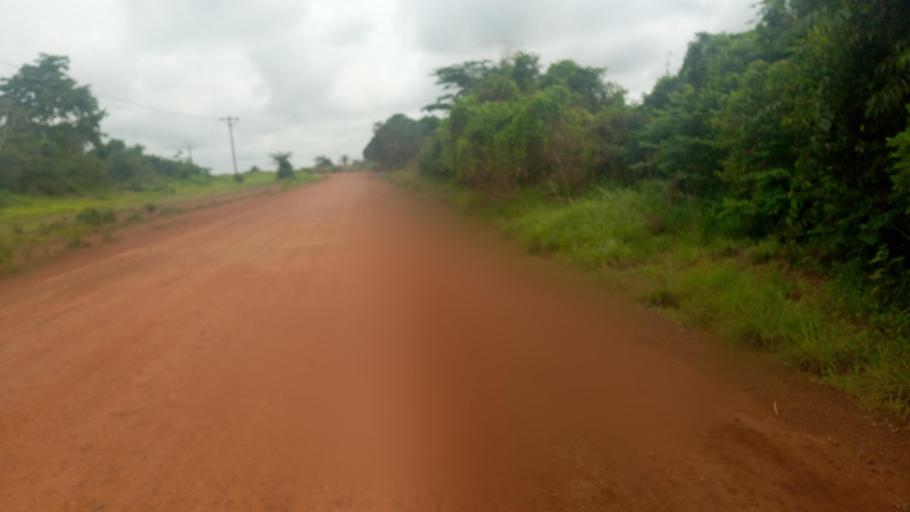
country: SL
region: Southern Province
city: Mogbwemo
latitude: 7.7350
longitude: -12.2790
